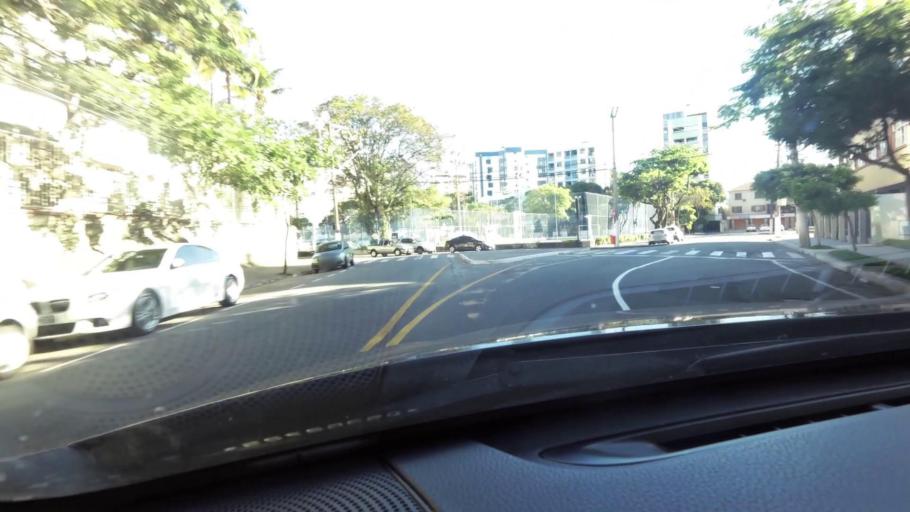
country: BR
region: Espirito Santo
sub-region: Vila Velha
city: Vila Velha
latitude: -20.3094
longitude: -40.2945
